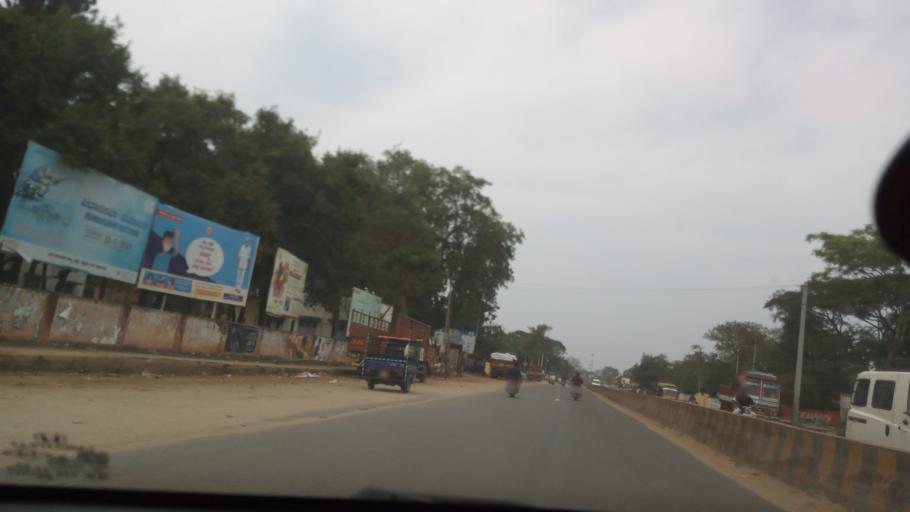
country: IN
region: Karnataka
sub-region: Chamrajnagar
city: Chamrajnagar
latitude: 11.9181
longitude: 76.9409
